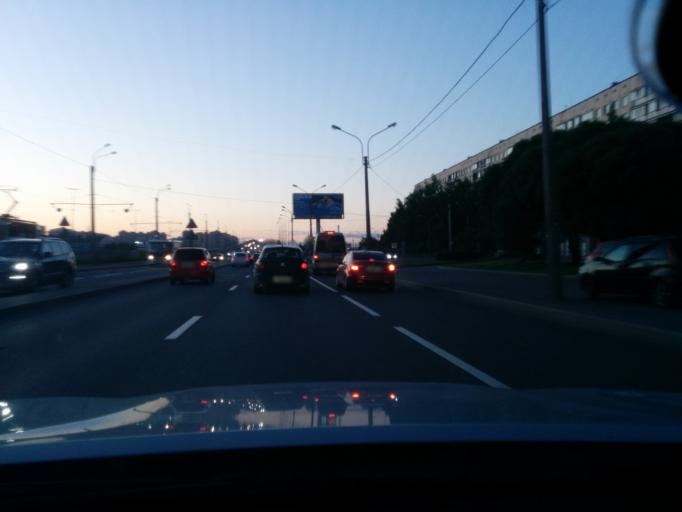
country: RU
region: Leningrad
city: Parnas
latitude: 60.0570
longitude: 30.3384
